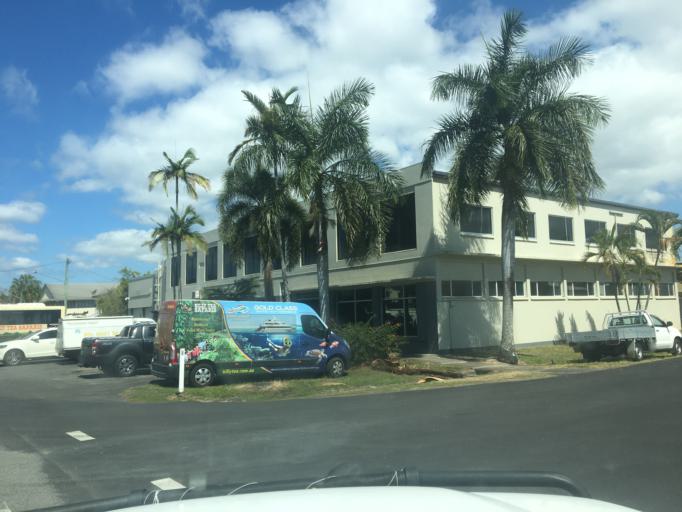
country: AU
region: Queensland
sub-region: Cairns
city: Cairns
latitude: -16.9248
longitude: 145.7670
